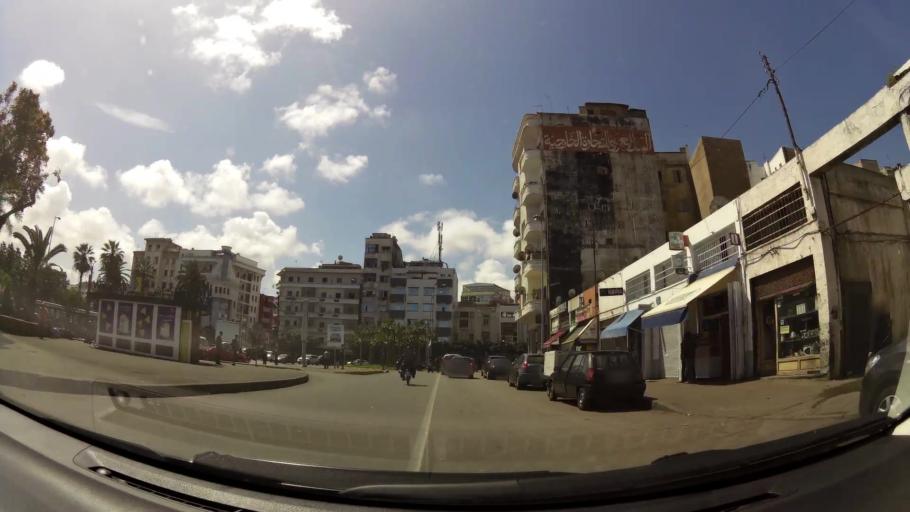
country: MA
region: Grand Casablanca
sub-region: Casablanca
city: Casablanca
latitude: 33.5961
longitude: -7.6246
